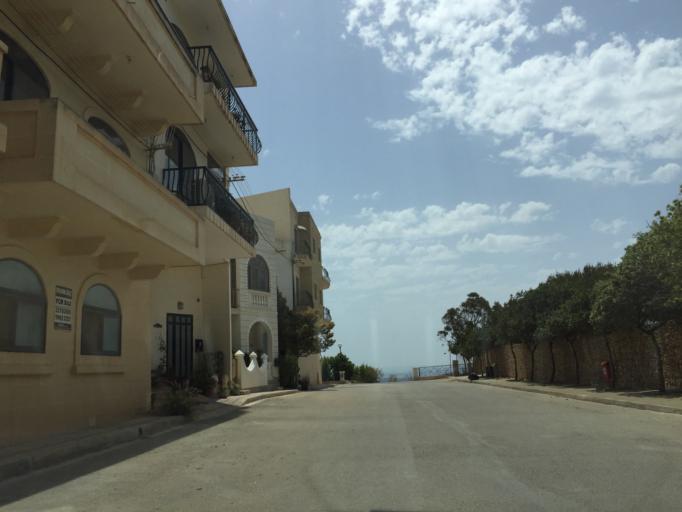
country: MT
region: Ghajnsielem
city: Ghajnsielem
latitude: 36.0360
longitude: 14.2841
